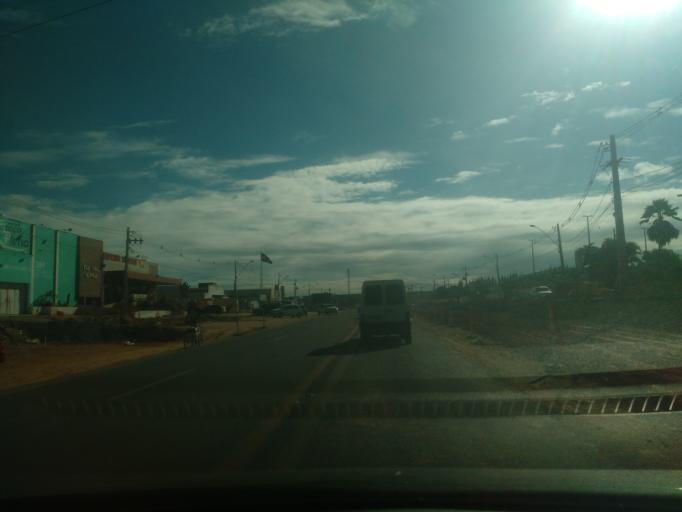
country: BR
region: Alagoas
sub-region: Satuba
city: Satuba
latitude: -9.5644
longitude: -35.7740
